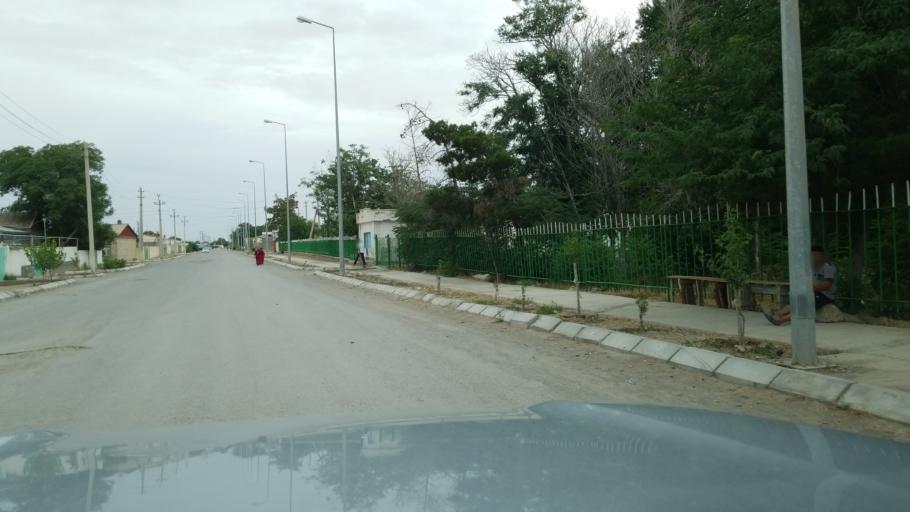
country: TM
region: Balkan
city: Serdar
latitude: 38.9807
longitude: 56.2748
